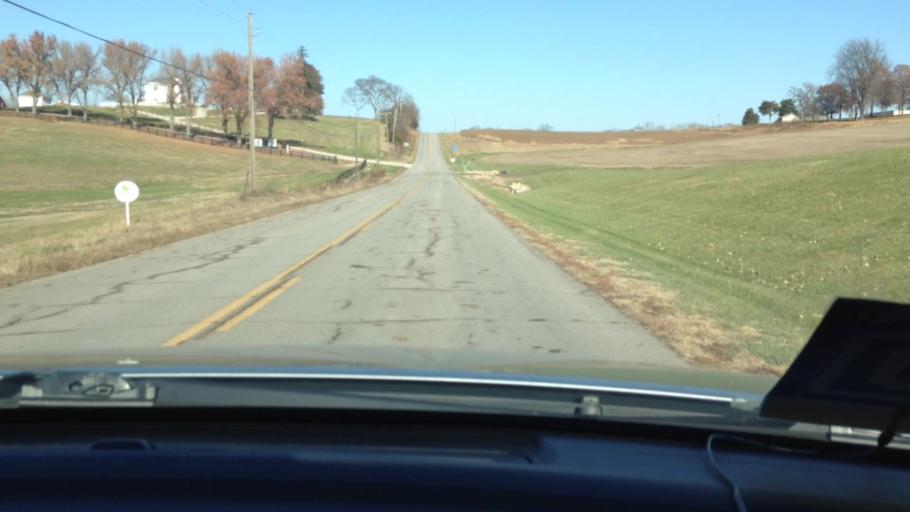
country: US
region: Missouri
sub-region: Platte County
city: Weston
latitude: 39.4305
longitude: -94.9007
